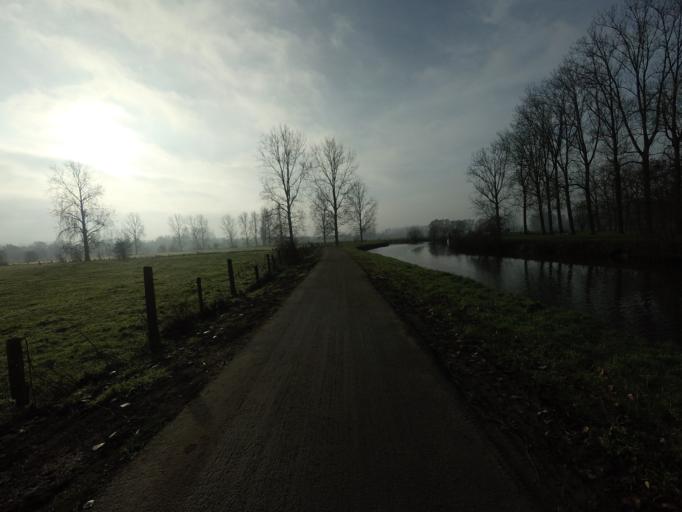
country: BE
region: Flanders
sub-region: Provincie Vlaams-Brabant
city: Galmaarden
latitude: 50.8006
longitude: 3.9561
